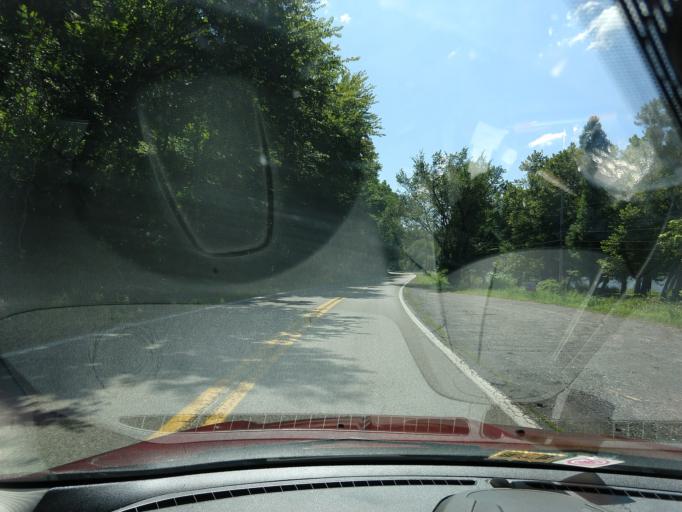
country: US
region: West Virginia
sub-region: Fayette County
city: Ansted
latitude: 38.1574
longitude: -81.1850
